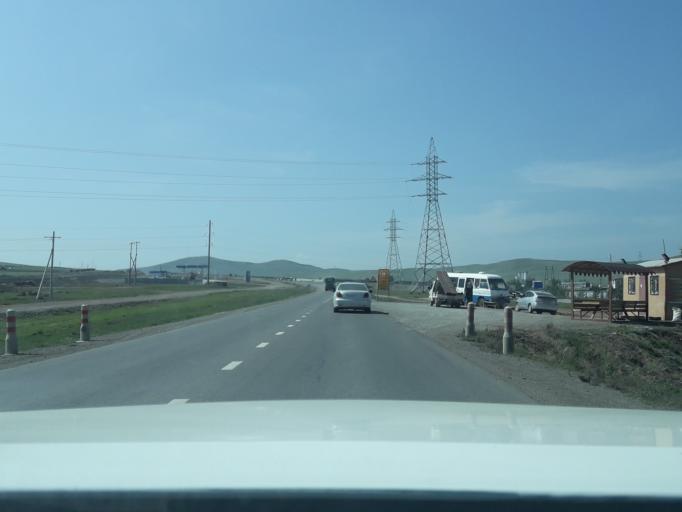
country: MN
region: Ulaanbaatar
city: Ulaanbaatar
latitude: 47.8198
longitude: 106.7600
